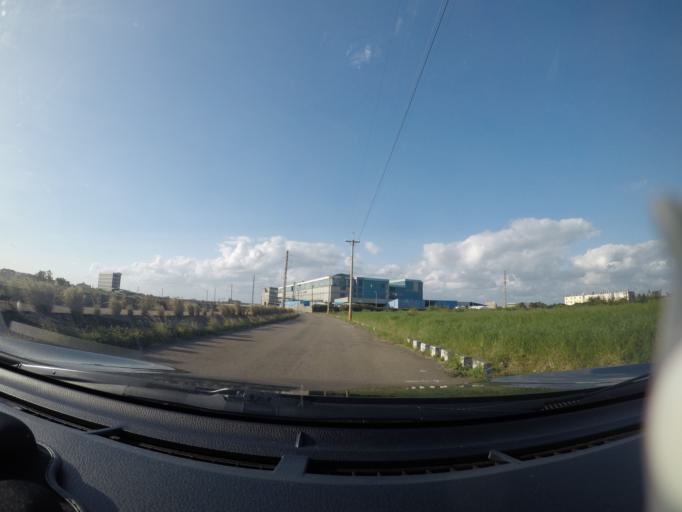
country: TW
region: Taiwan
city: Taoyuan City
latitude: 25.1060
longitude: 121.2517
